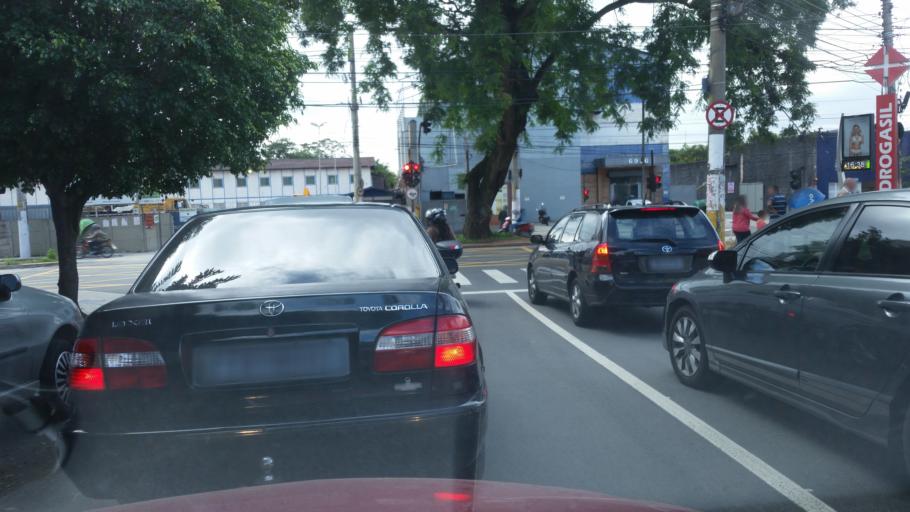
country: BR
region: Sao Paulo
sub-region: Diadema
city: Diadema
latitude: -23.6413
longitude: -46.6986
